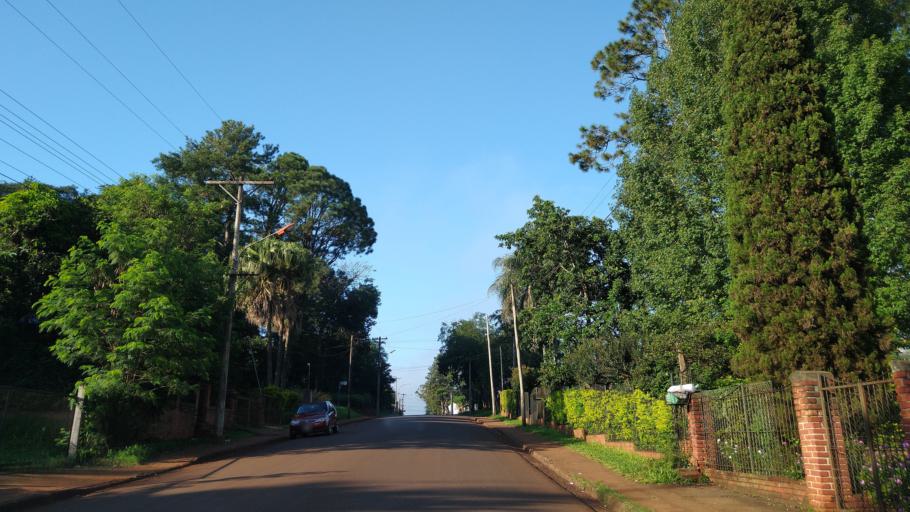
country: AR
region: Misiones
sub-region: Departamento de Montecarlo
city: Montecarlo
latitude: -26.5654
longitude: -54.7727
